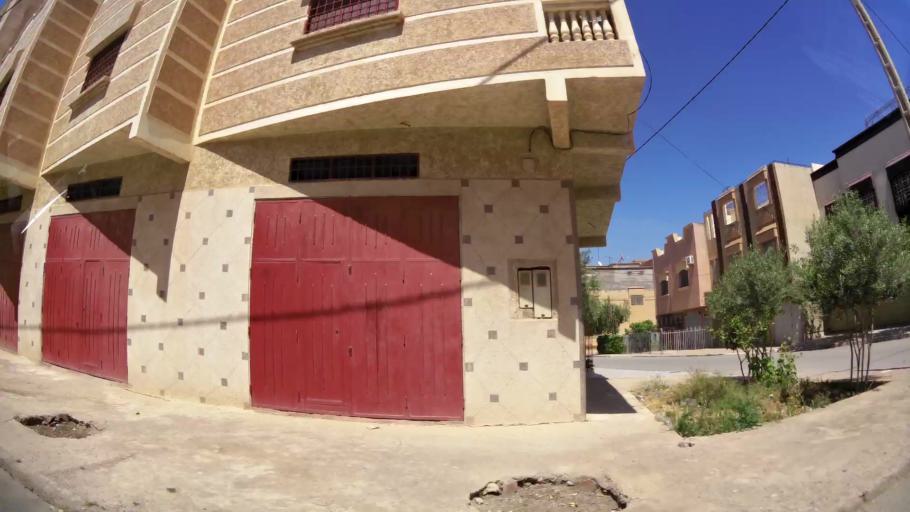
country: MA
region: Oriental
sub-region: Oujda-Angad
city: Oujda
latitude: 34.6925
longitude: -1.8835
